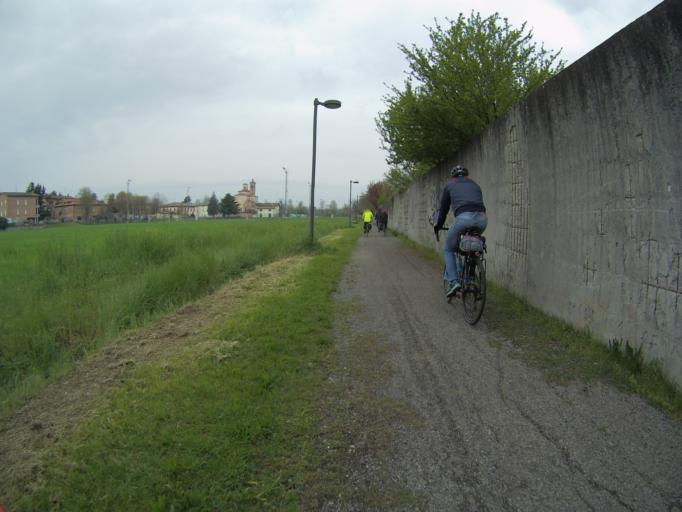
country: IT
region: Emilia-Romagna
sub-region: Provincia di Reggio Emilia
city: Reggio nell'Emilia
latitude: 44.6808
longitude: 10.5940
